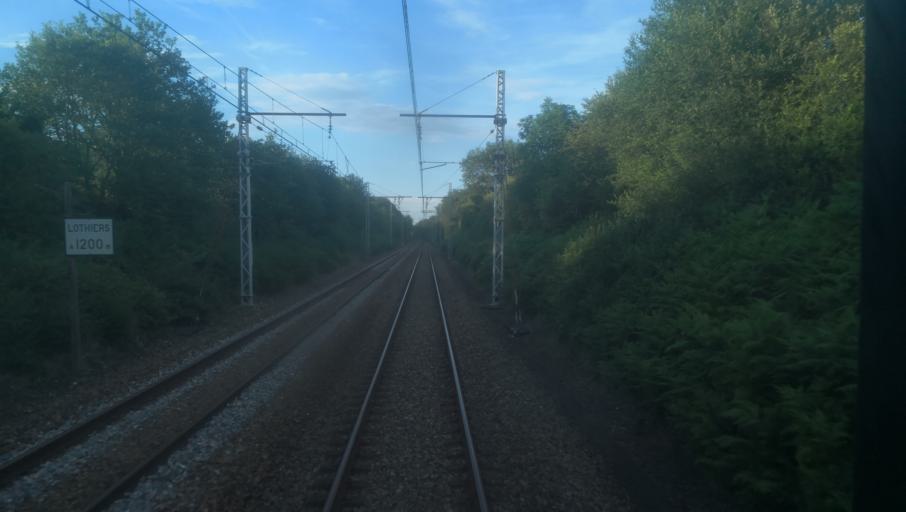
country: FR
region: Centre
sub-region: Departement de l'Indre
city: Luant
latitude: 46.6846
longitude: 1.5554
